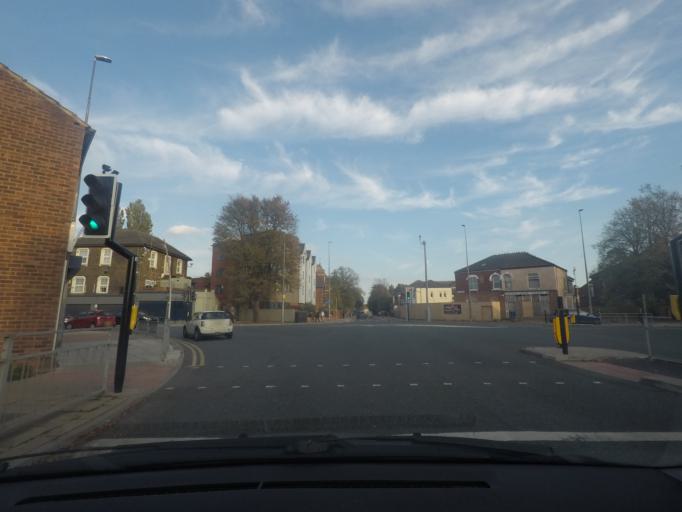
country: GB
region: England
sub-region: North East Lincolnshire
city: Grimsby
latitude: 53.5673
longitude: -0.0752
